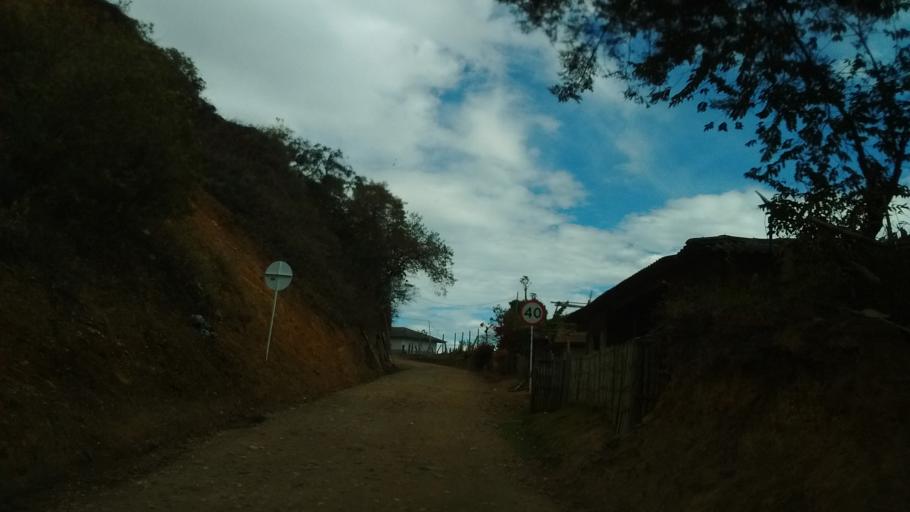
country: CO
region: Cauca
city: Almaguer
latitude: 1.8442
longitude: -76.8970
